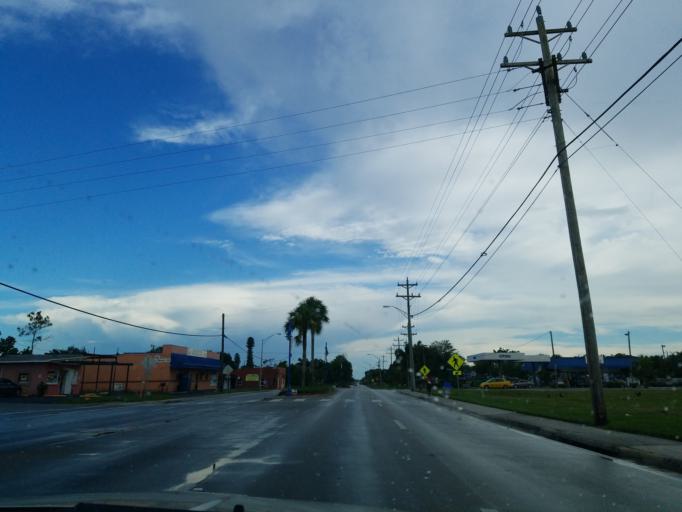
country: US
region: Florida
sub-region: Collier County
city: Immokalee
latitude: 26.4138
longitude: -81.4174
